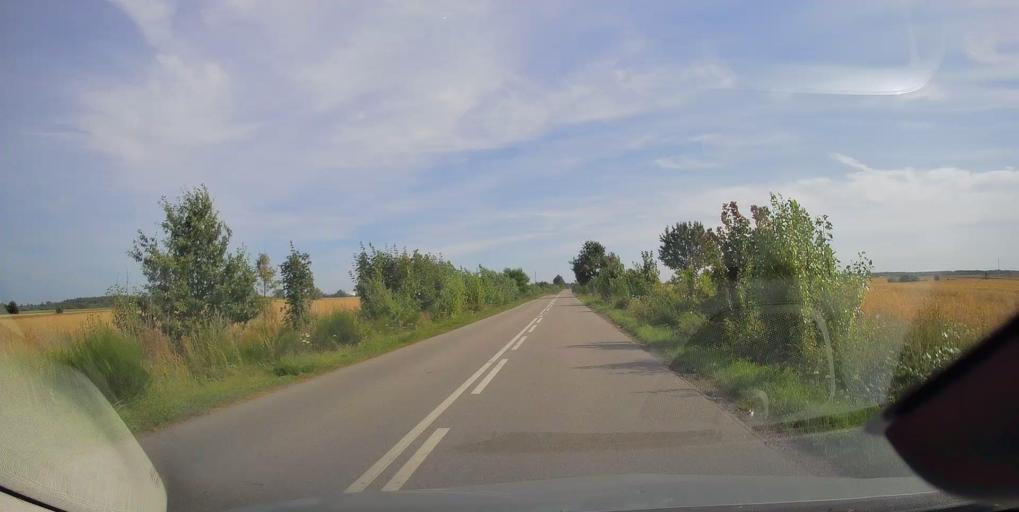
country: PL
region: Lodz Voivodeship
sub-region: Powiat opoczynski
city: Mniszkow
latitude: 51.3865
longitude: 20.0342
